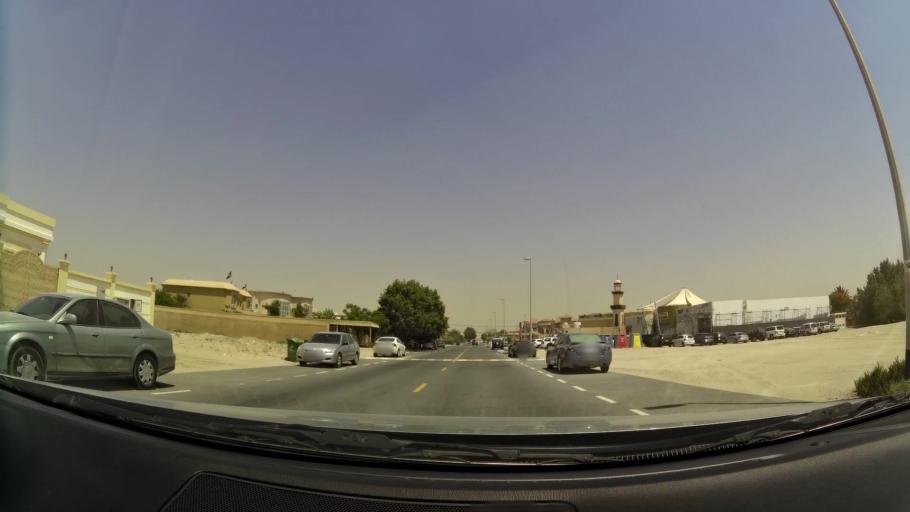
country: AE
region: Dubai
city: Dubai
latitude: 25.0955
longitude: 55.2138
